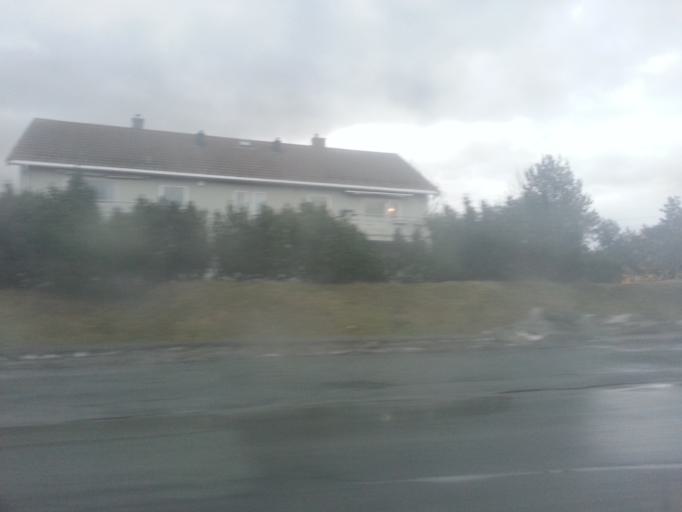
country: NO
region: Sor-Trondelag
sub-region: Trondheim
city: Trondheim
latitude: 63.4304
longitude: 10.4547
